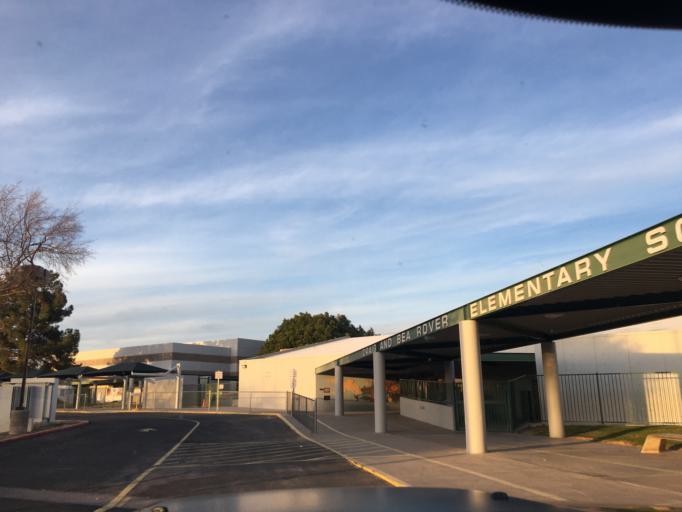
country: US
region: Arizona
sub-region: Maricopa County
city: Guadalupe
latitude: 33.3693
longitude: -111.9185
